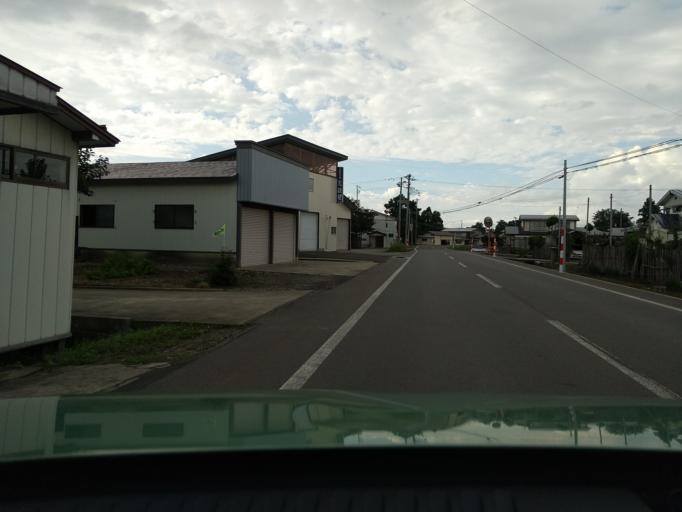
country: JP
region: Akita
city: Yokotemachi
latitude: 39.3279
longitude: 140.4858
